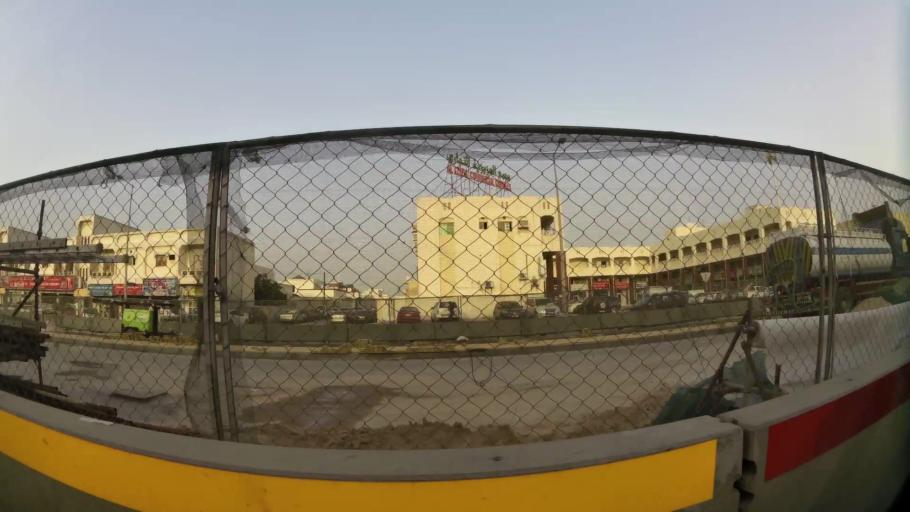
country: QA
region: Baladiyat ar Rayyan
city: Ar Rayyan
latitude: 25.2494
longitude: 51.4519
